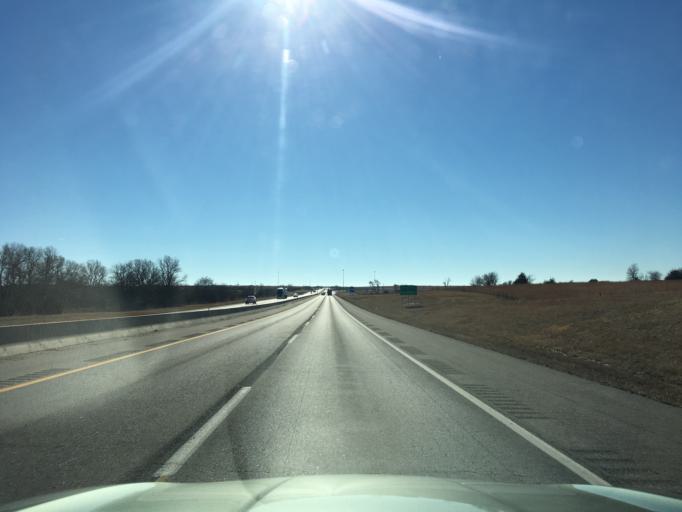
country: US
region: Kansas
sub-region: Sumner County
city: Wellington
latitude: 37.0679
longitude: -97.3385
